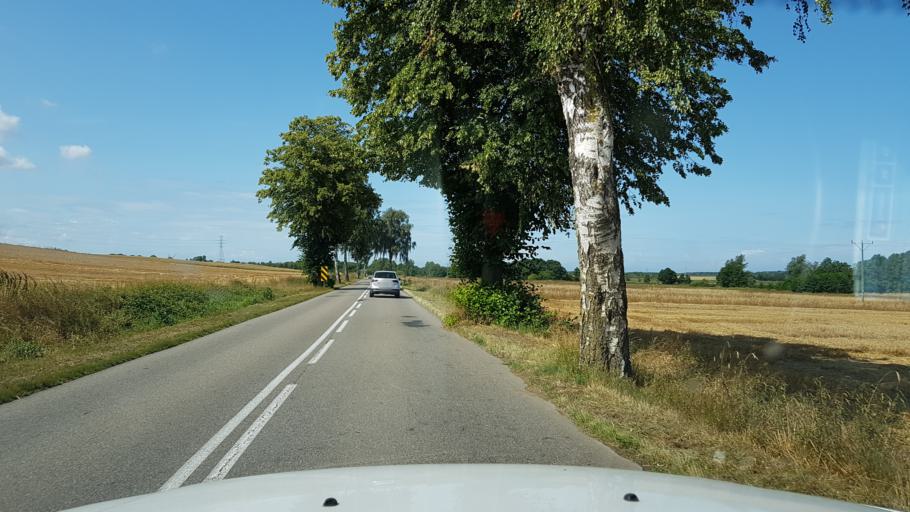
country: PL
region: West Pomeranian Voivodeship
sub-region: Powiat gryficki
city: Karnice
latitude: 54.0730
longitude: 15.0966
